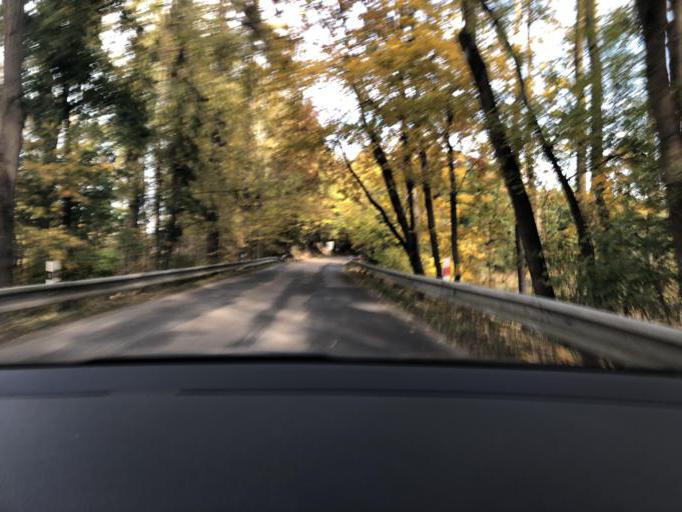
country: CZ
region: Central Bohemia
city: Postupice
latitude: 49.7772
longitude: 14.8010
